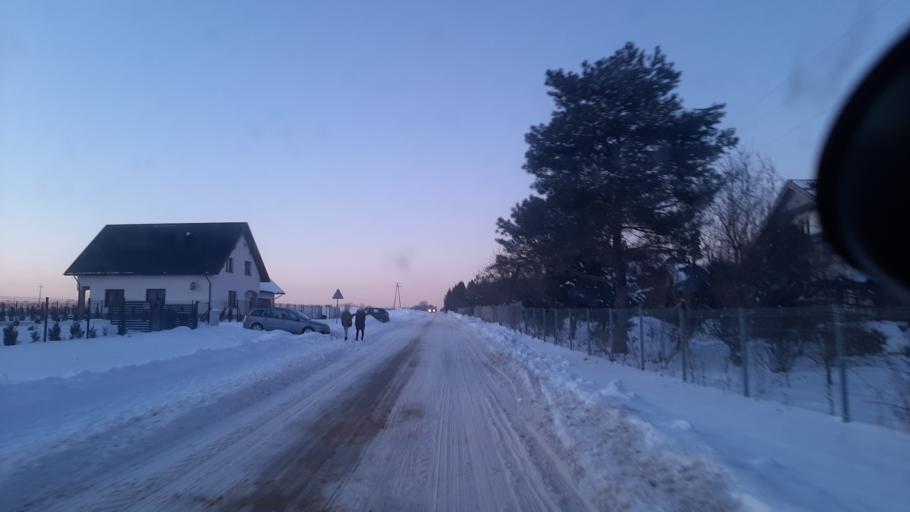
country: PL
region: Lublin Voivodeship
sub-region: Powiat lubelski
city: Jastkow
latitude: 51.3638
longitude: 22.5287
